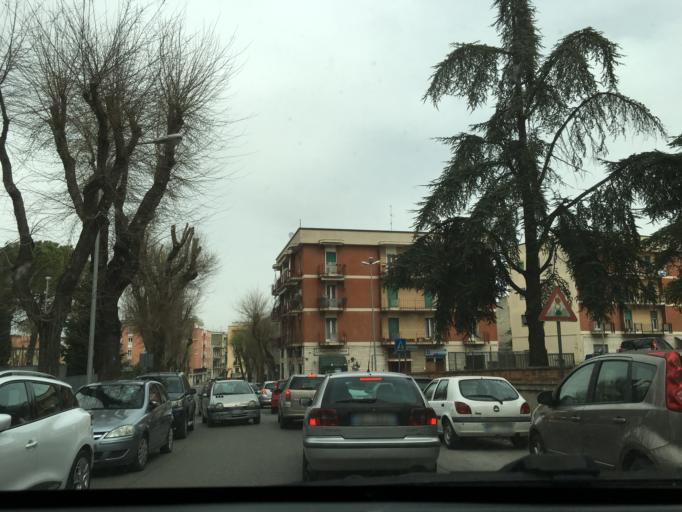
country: IT
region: Basilicate
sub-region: Provincia di Matera
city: Matera
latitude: 40.6727
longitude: 16.5983
